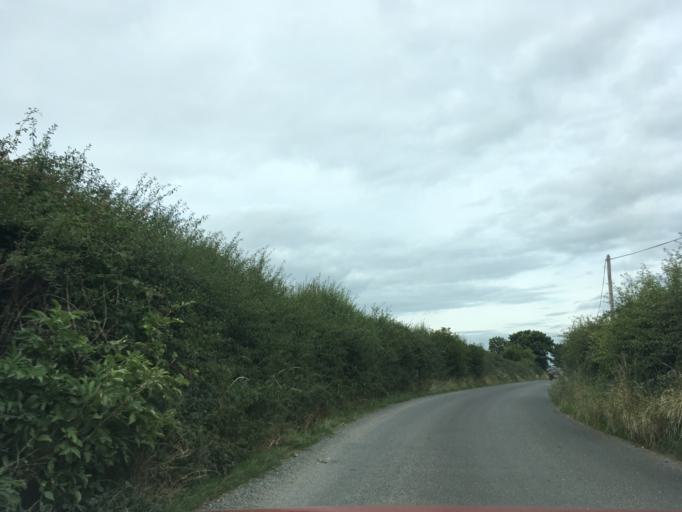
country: IE
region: Munster
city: Cahir
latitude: 52.4699
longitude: -8.0028
